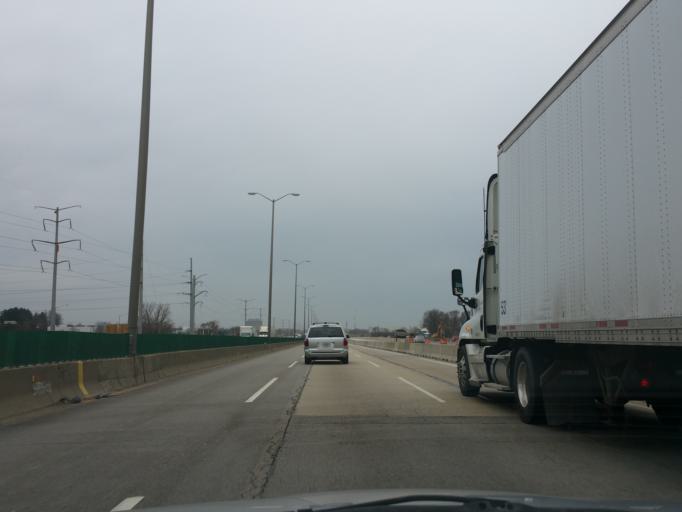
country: US
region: Illinois
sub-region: Cook County
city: Hoffman Estates
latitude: 42.0606
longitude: -88.0525
